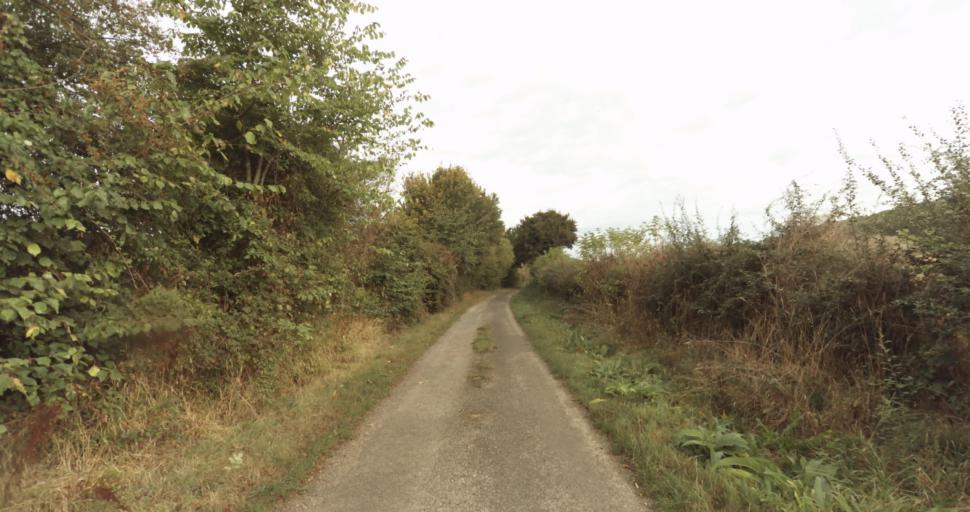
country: FR
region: Lower Normandy
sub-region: Departement de l'Orne
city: Vimoutiers
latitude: 48.9418
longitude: 0.2752
